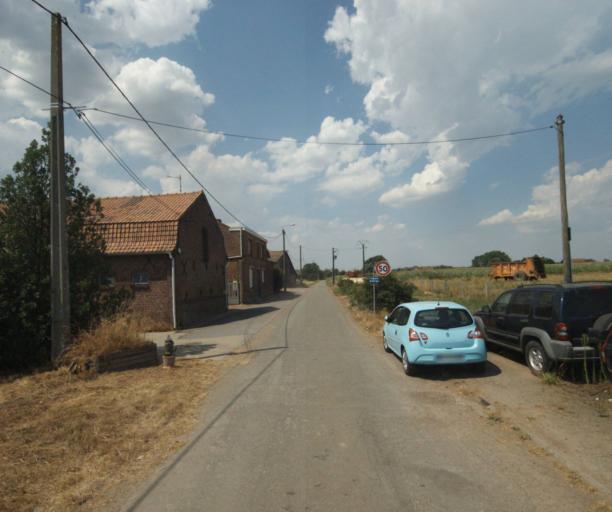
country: FR
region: Nord-Pas-de-Calais
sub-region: Departement du Nord
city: Comines
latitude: 50.7509
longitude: 2.9833
